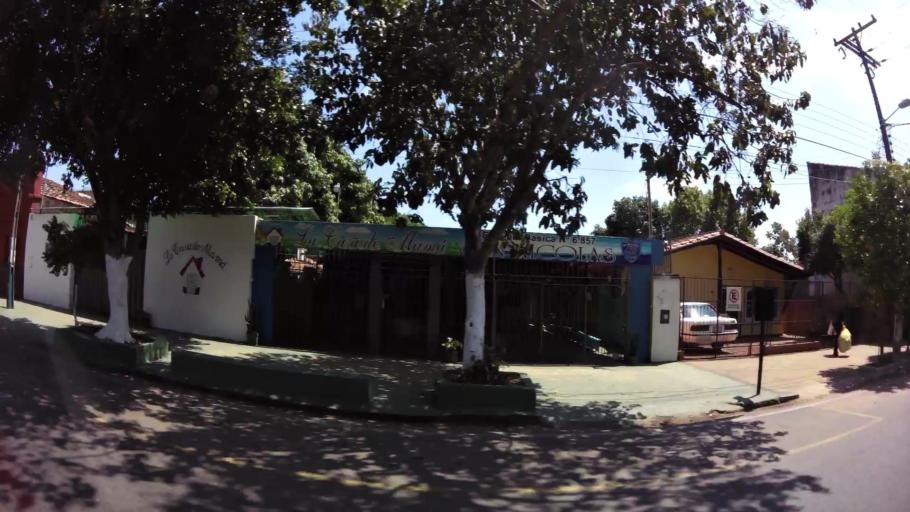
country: PY
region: Central
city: San Lorenzo
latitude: -25.3500
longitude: -57.5120
